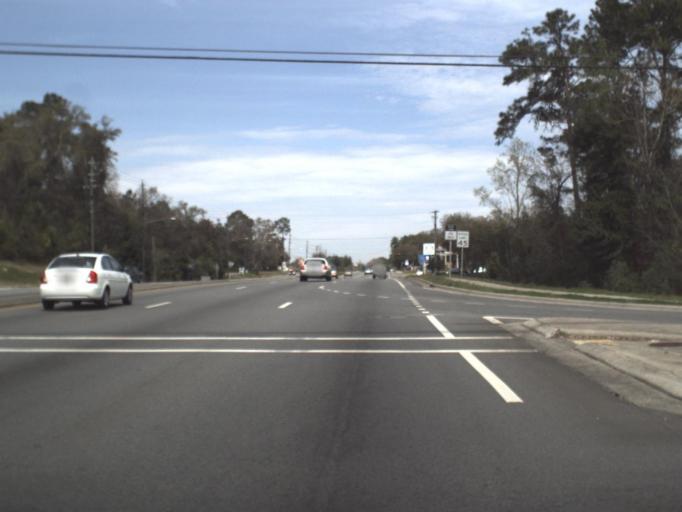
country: US
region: Florida
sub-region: Leon County
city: Tallahassee
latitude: 30.4633
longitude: -84.3610
